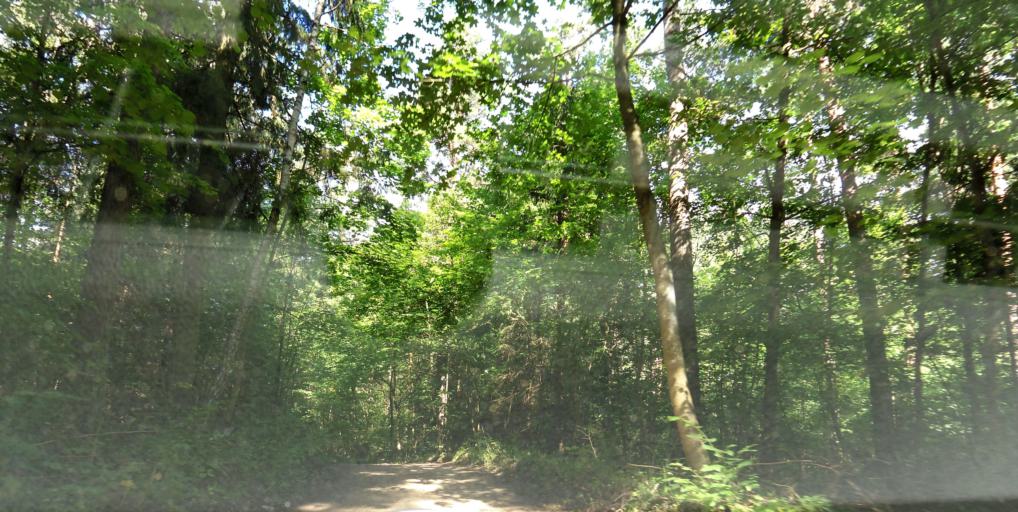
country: LT
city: Grigiskes
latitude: 54.7408
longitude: 25.0297
